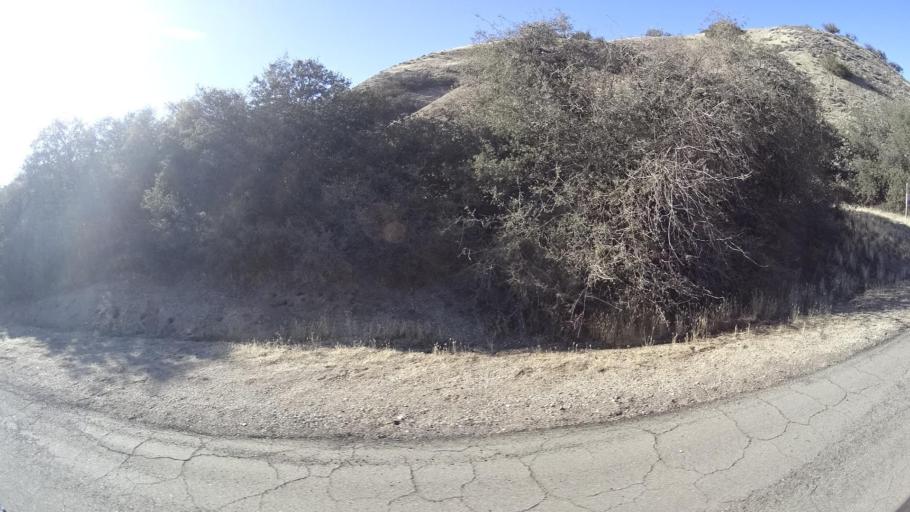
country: US
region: California
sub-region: Kern County
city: Maricopa
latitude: 34.9461
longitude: -119.4011
